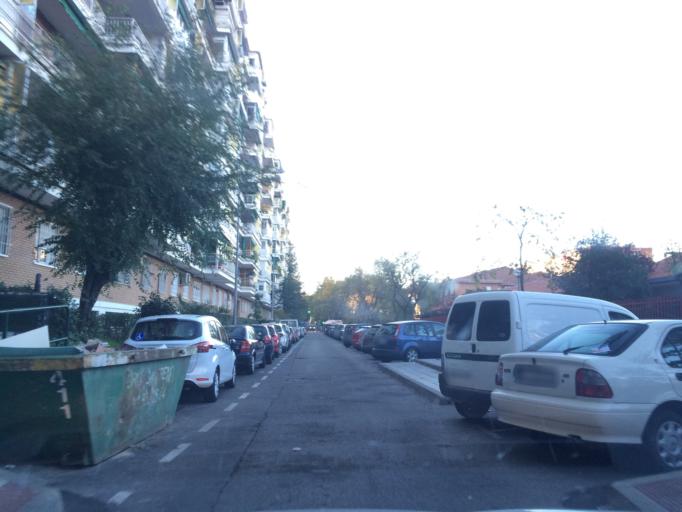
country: ES
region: Madrid
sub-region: Provincia de Madrid
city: Alcorcon
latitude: 40.3520
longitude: -3.8146
